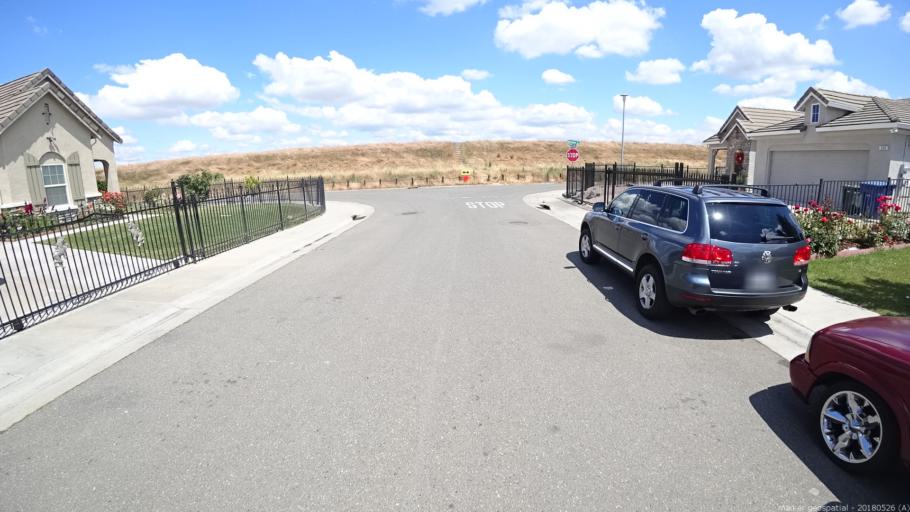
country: US
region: California
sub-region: Sacramento County
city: Sacramento
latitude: 38.6246
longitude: -121.4709
